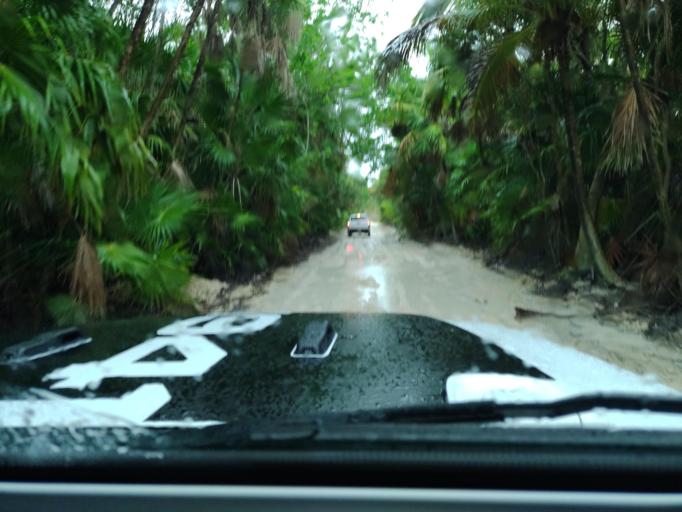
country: MX
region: Quintana Roo
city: Tulum
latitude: 19.9738
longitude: -87.4689
